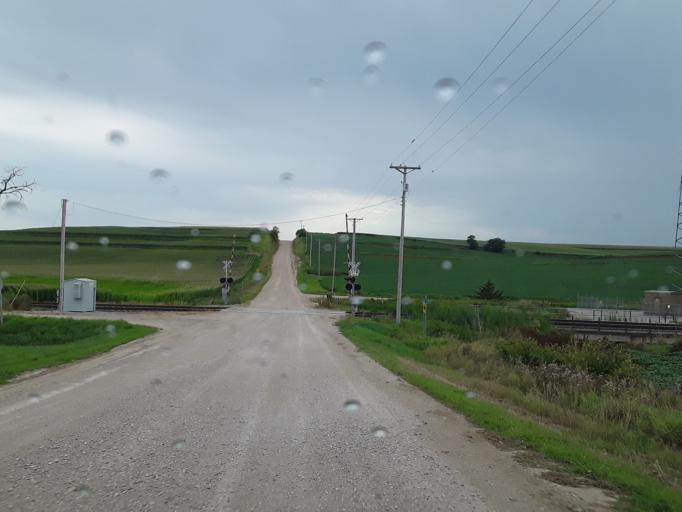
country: US
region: Nebraska
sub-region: Washington County
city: Blair
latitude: 41.5092
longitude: -96.1731
